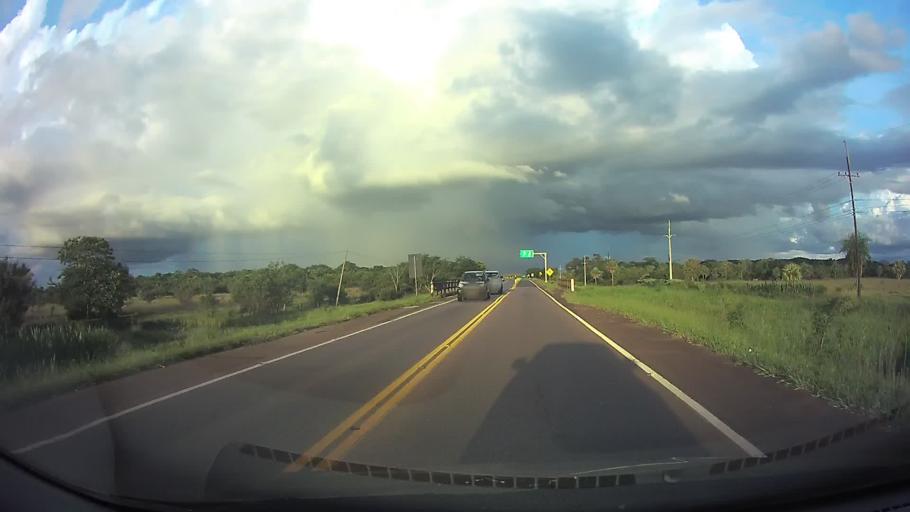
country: PY
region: Paraguari
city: Carapegua
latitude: -25.7511
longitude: -57.2208
